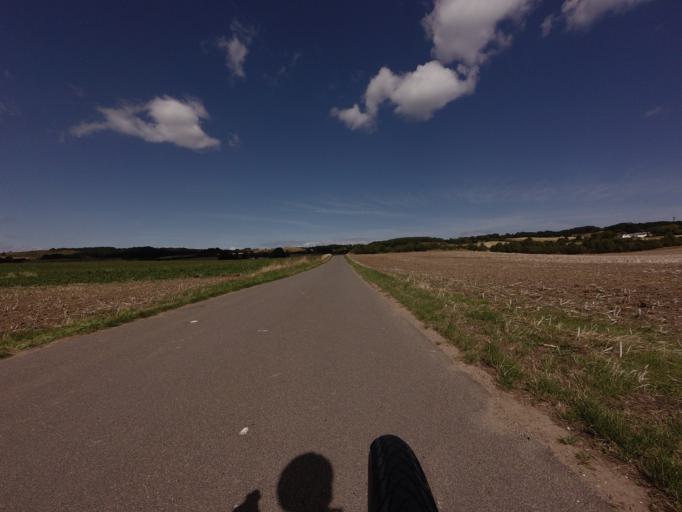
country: DK
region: Zealand
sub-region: Vordingborg Kommune
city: Stege
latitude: 54.9497
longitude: 12.5324
